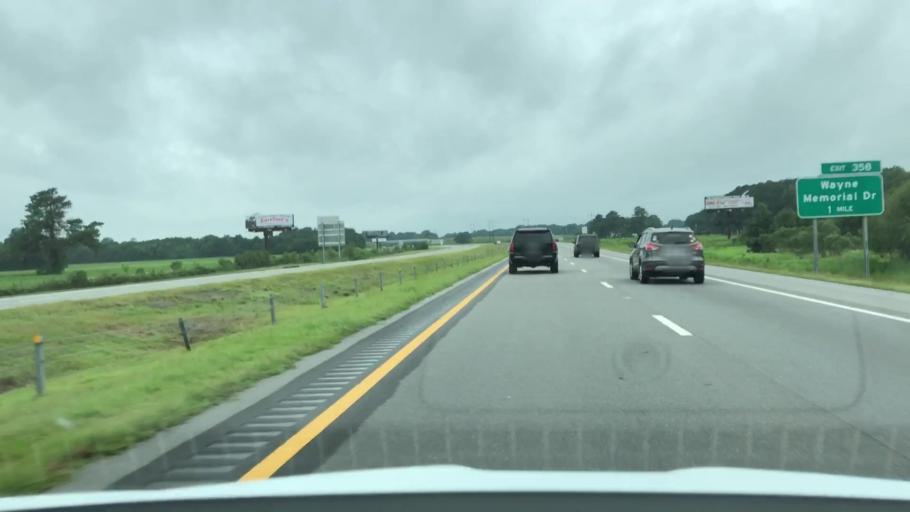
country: US
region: North Carolina
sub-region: Wayne County
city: Elroy
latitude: 35.4167
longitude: -77.9104
